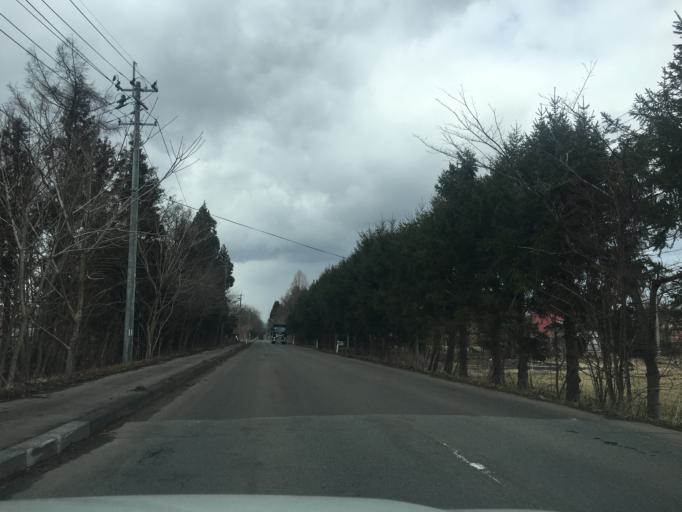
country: JP
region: Akita
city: Takanosu
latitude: 40.1784
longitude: 140.3468
